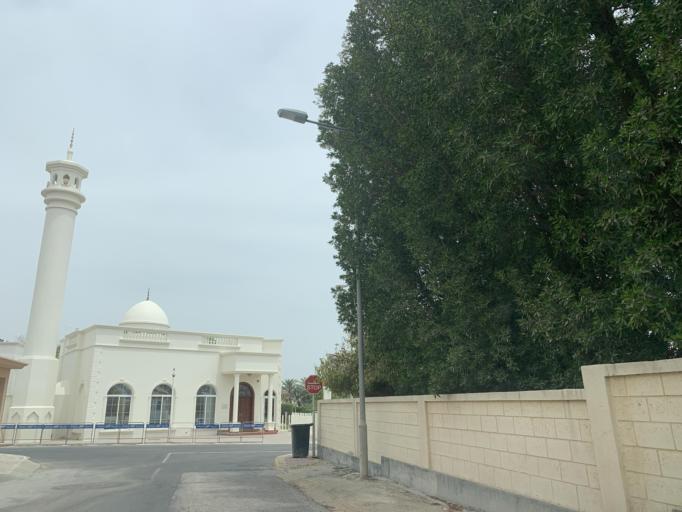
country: BH
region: Northern
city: Ar Rifa'
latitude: 26.1364
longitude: 50.5461
